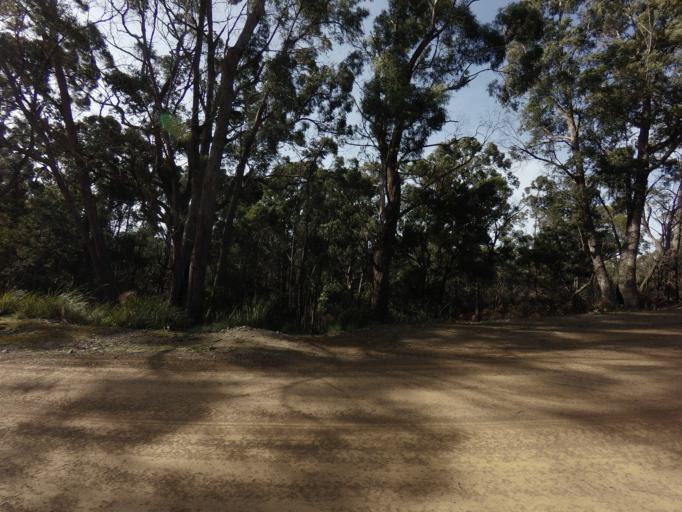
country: AU
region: Tasmania
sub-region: Kingborough
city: Margate
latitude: -43.0783
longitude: 147.2653
